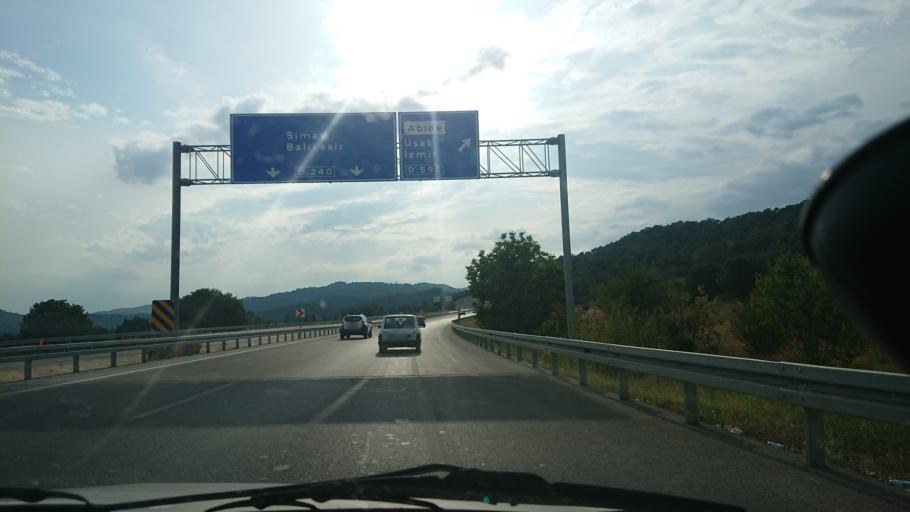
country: TR
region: Kuetahya
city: Gediz
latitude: 38.9356
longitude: 29.3131
